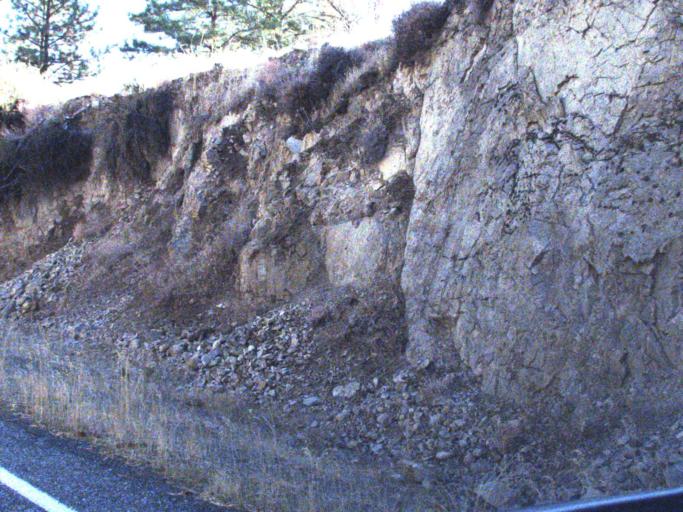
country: US
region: Washington
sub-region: Okanogan County
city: Coulee Dam
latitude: 47.9767
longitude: -118.6977
